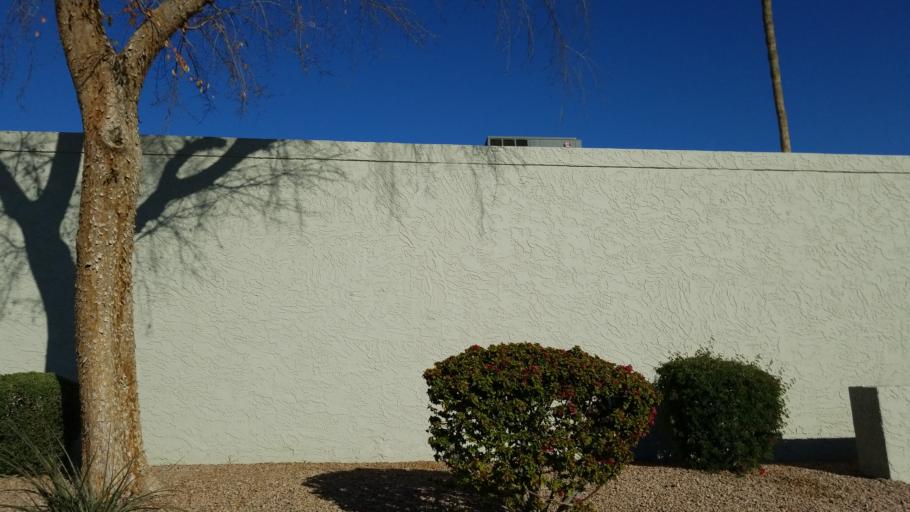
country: US
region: Arizona
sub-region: Maricopa County
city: Phoenix
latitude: 33.5115
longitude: -112.0628
